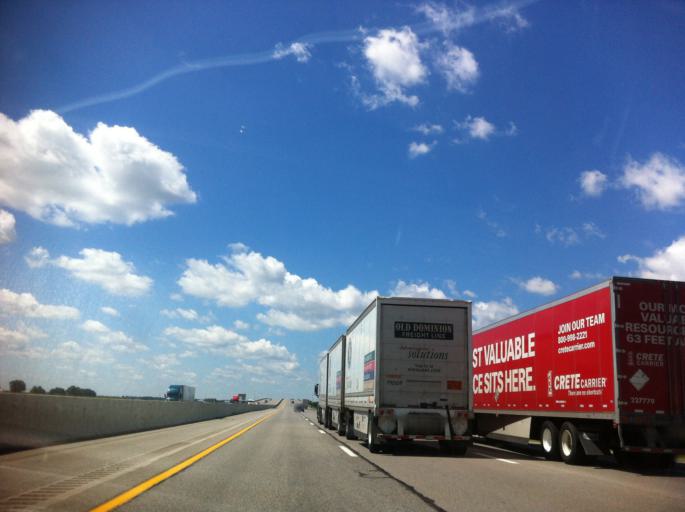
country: US
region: Ohio
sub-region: Wood County
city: Walbridge
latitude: 41.5385
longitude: -83.4992
